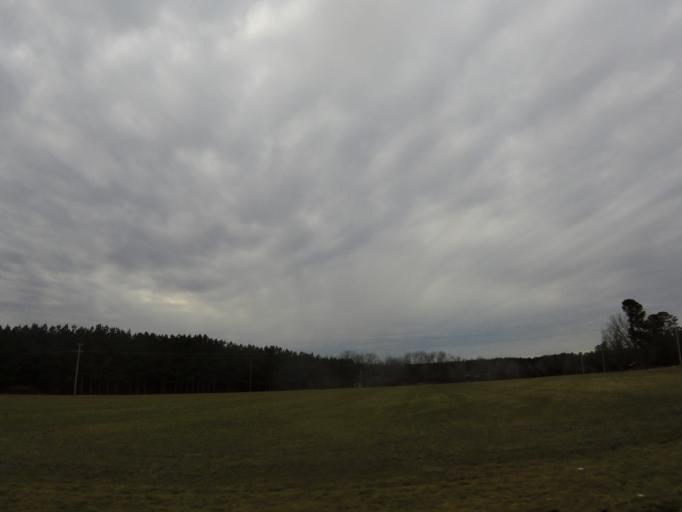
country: US
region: North Carolina
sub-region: Northampton County
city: Jackson
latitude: 36.2882
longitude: -77.2760
